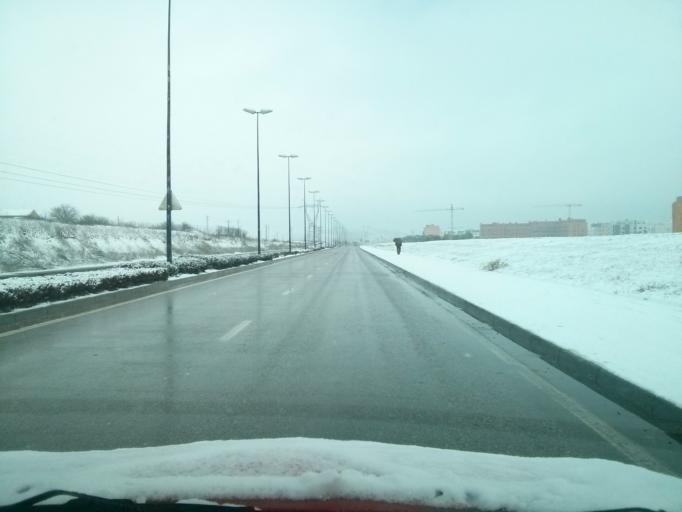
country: ES
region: Castille and Leon
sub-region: Provincia de Burgos
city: Burgos
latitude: 42.3667
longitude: -3.6714
